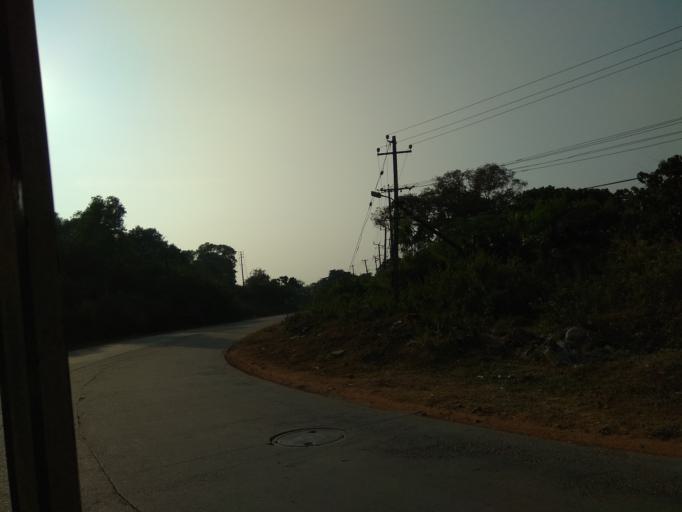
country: IN
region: Karnataka
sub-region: Dakshina Kannada
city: Mangalore
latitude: 12.9168
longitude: 74.8581
